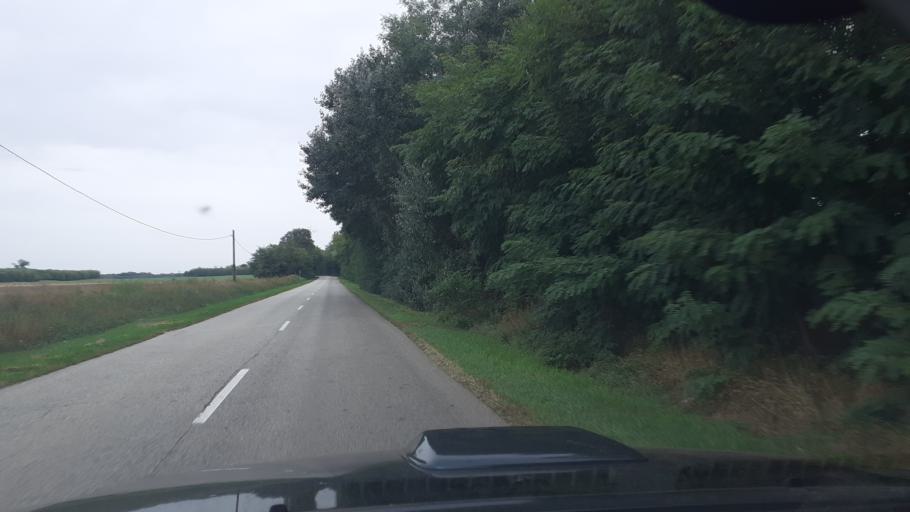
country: HU
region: Fejer
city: Baracs
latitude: 46.8425
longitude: 18.8920
